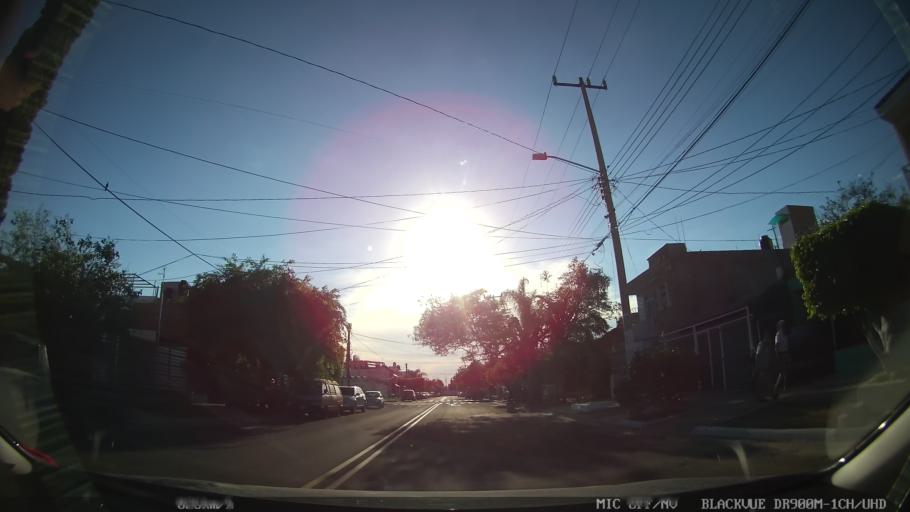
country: MX
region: Jalisco
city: Tlaquepaque
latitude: 20.7010
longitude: -103.2984
